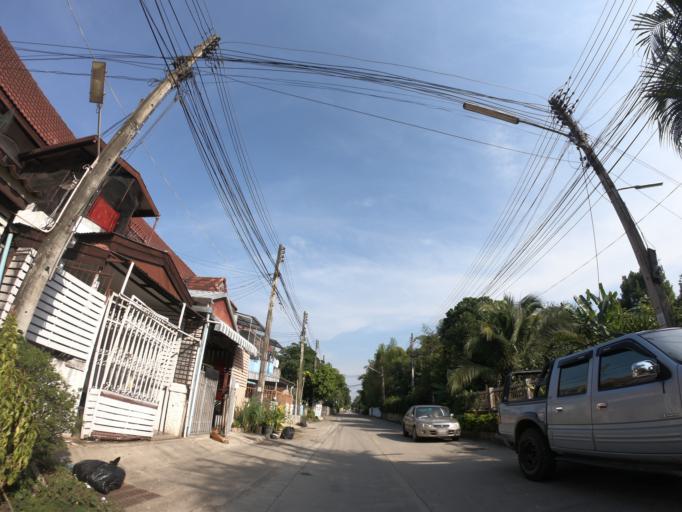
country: TH
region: Chiang Mai
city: Chiang Mai
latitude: 18.8181
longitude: 98.9902
